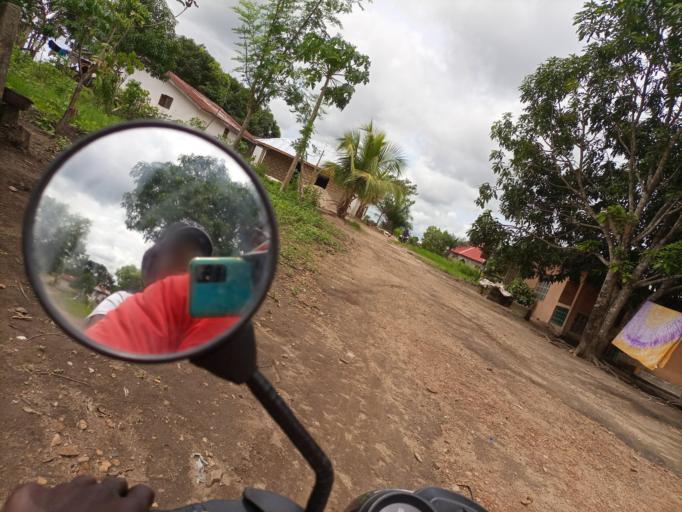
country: SL
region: Southern Province
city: Baoma
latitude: 7.9685
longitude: -11.7114
